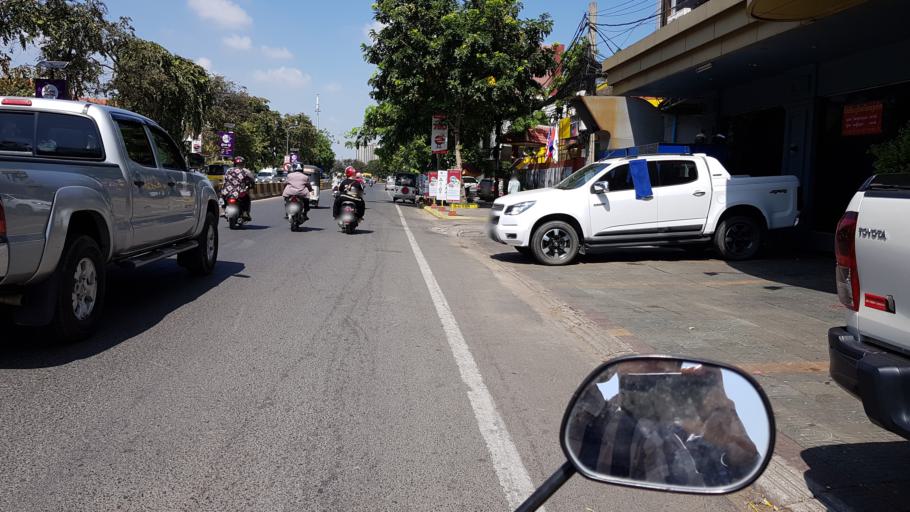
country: KH
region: Phnom Penh
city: Phnom Penh
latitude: 11.5683
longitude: 104.9113
